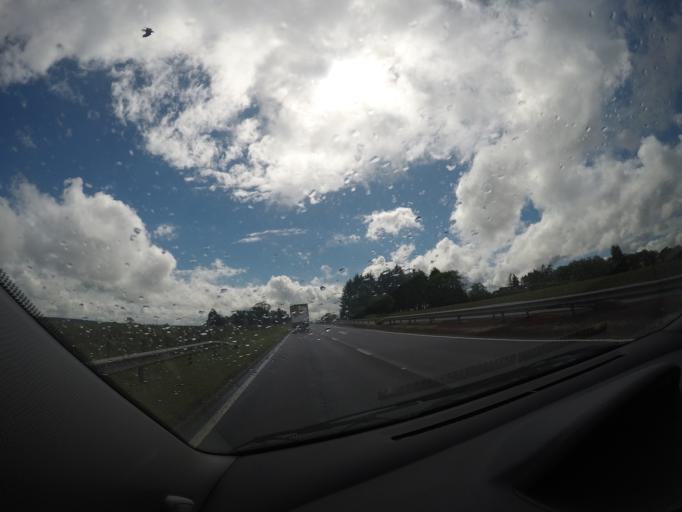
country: GB
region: Scotland
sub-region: Stirling
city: Dunblane
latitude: 56.2275
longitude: -3.9118
